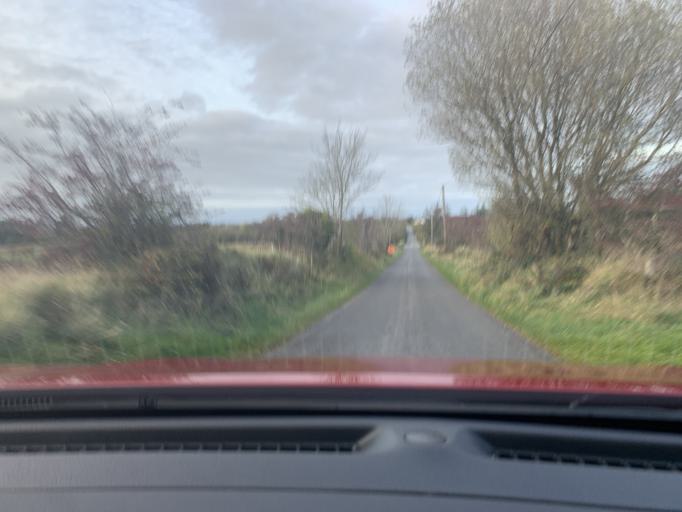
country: IE
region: Connaught
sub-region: Roscommon
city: Ballaghaderreen
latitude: 53.9791
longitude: -8.6176
